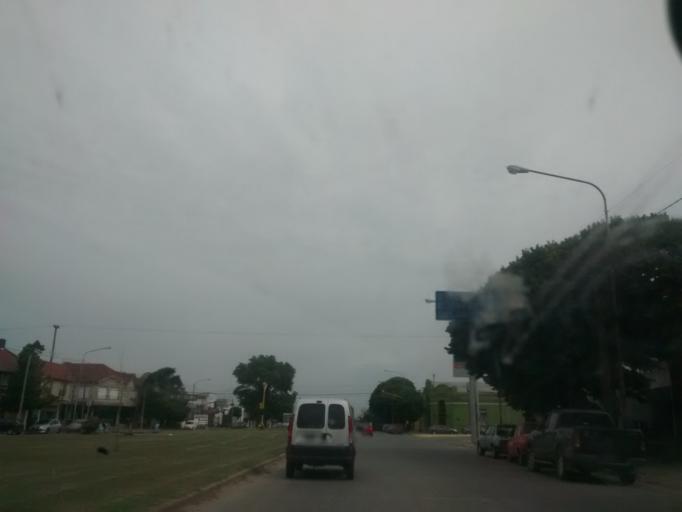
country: AR
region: Buenos Aires
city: Necochea
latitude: -38.5670
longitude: -58.7228
